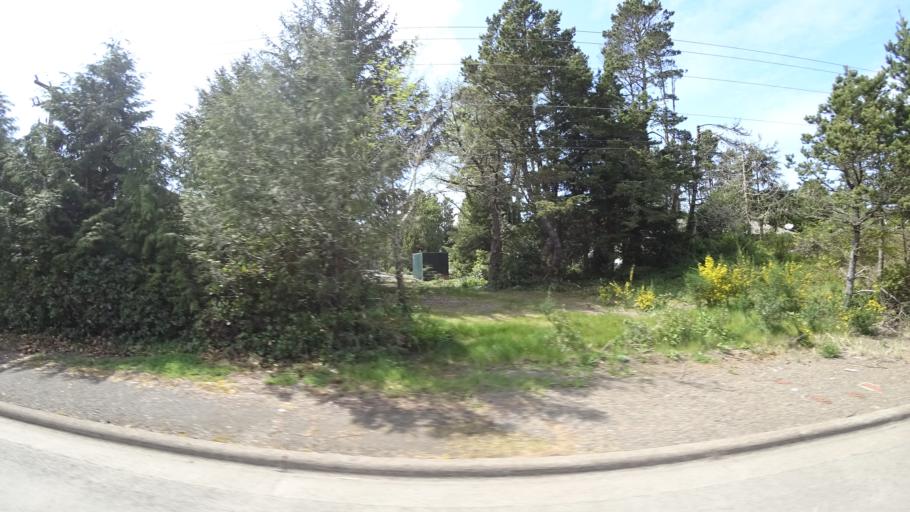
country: US
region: Oregon
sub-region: Lincoln County
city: Lincoln Beach
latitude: 44.8638
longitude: -124.0368
